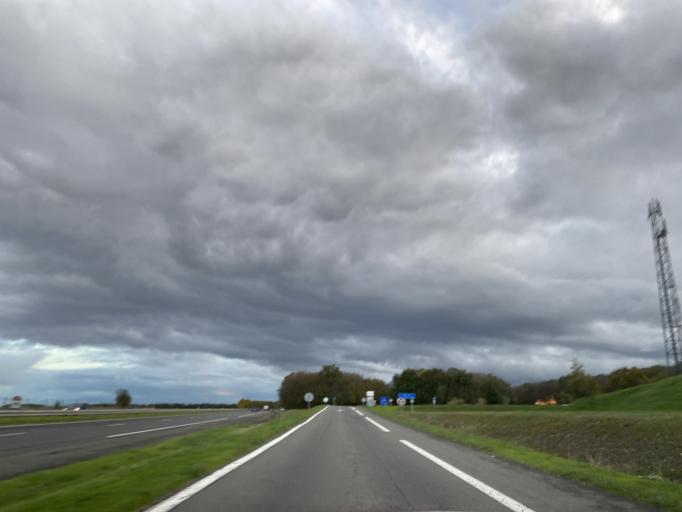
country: FR
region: Centre
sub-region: Departement du Cher
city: Plaimpied-Givaudins
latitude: 46.9843
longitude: 2.4143
